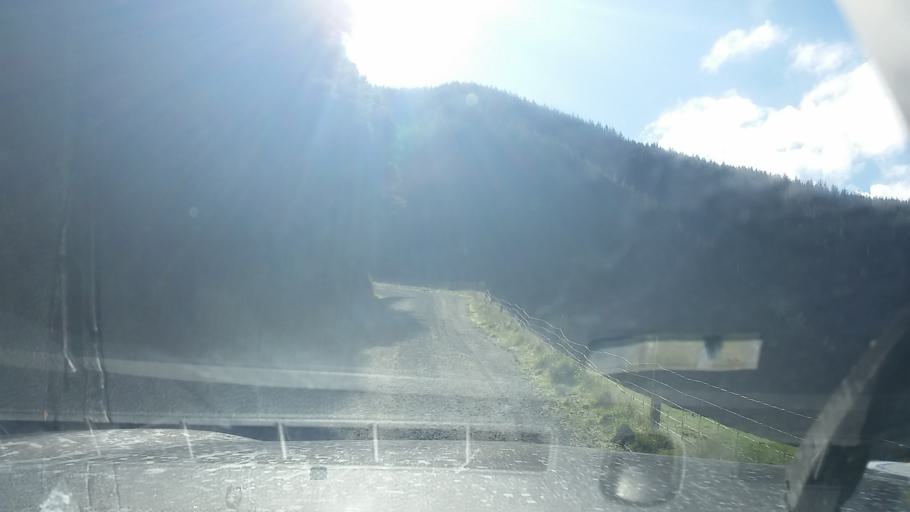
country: NZ
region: Marlborough
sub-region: Marlborough District
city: Picton
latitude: -41.1437
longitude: 174.0508
